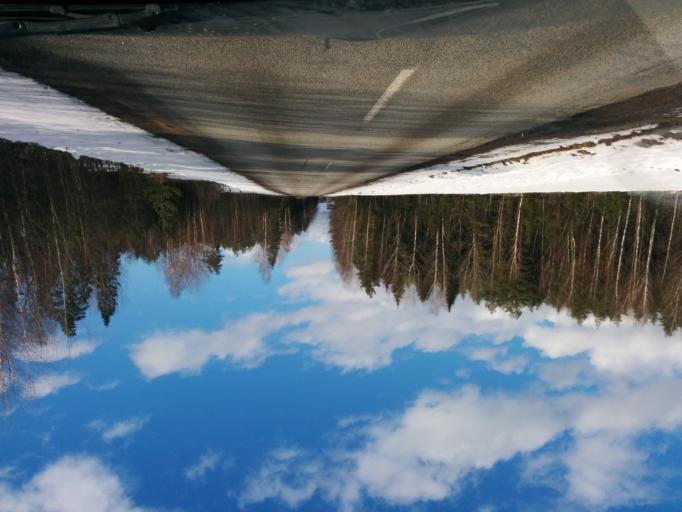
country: LV
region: Aluksnes Rajons
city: Aluksne
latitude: 57.1929
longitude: 26.9933
